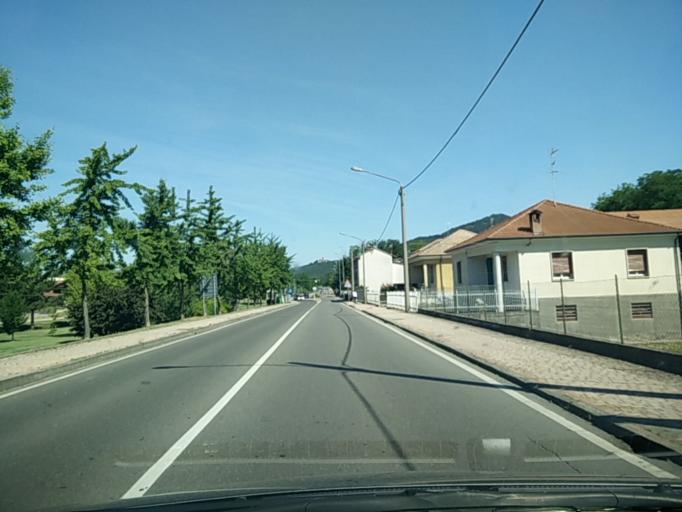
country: IT
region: Lombardy
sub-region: Provincia di Pavia
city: Godiasco
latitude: 44.8977
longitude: 9.0544
